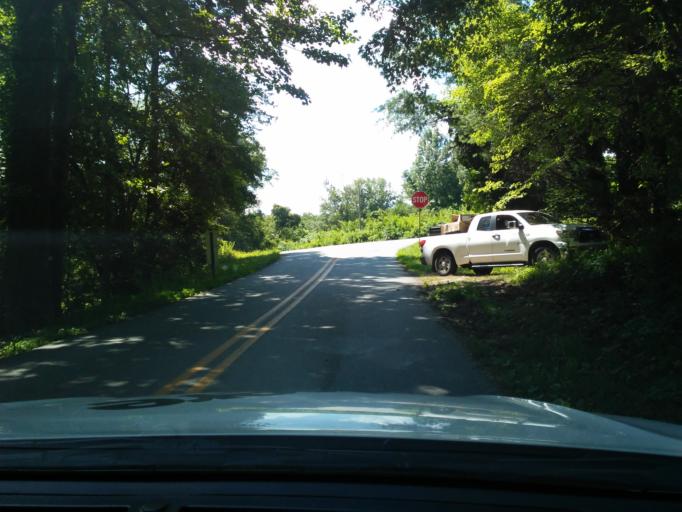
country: US
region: Georgia
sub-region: Union County
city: Blairsville
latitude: 34.9361
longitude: -83.8775
